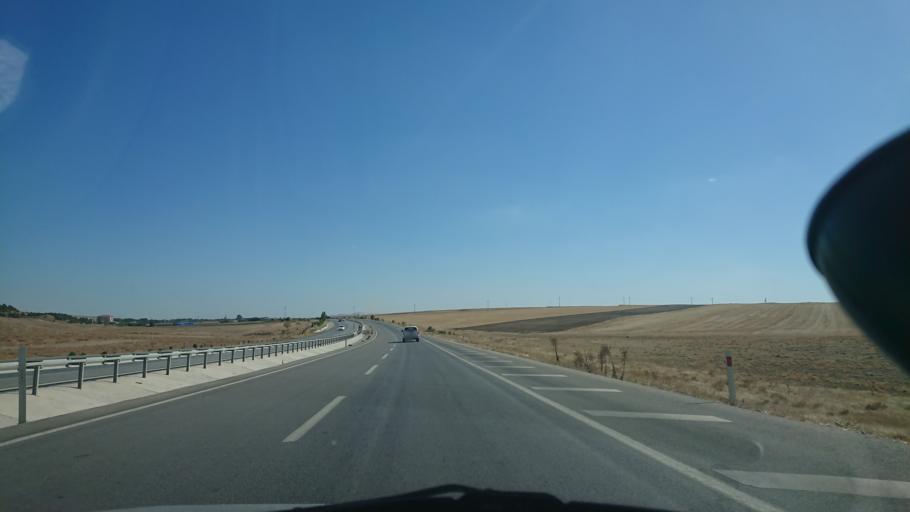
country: TR
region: Eskisehir
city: Mahmudiye
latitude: 39.5015
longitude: 30.9674
